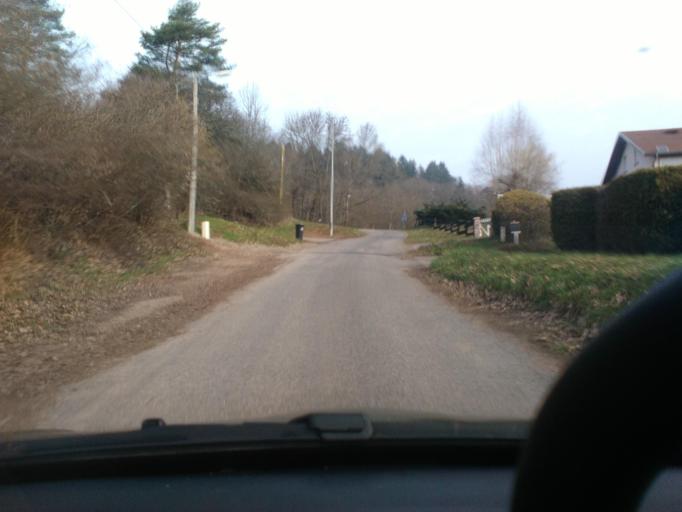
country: FR
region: Lorraine
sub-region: Departement des Vosges
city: Saint-Die-des-Vosges
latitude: 48.3010
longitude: 6.9467
